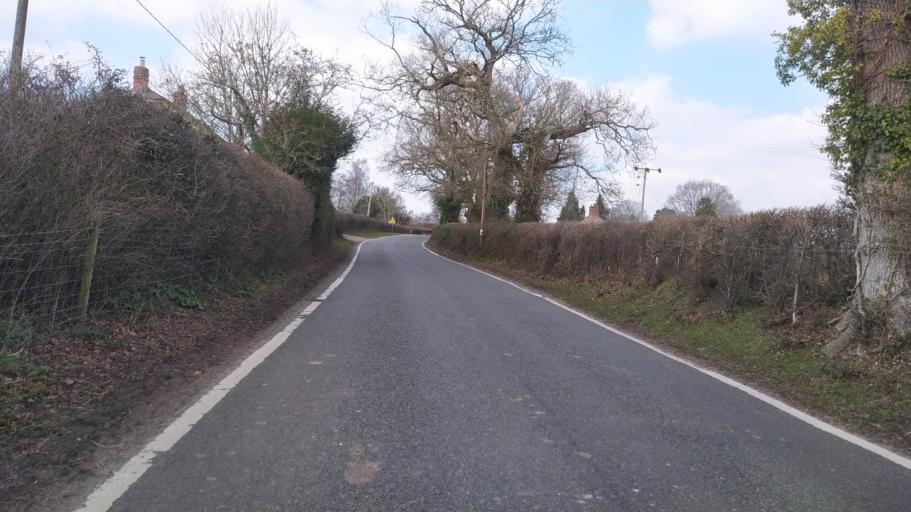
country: GB
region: England
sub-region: Hampshire
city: Cadnam
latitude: 50.9361
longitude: -1.6169
